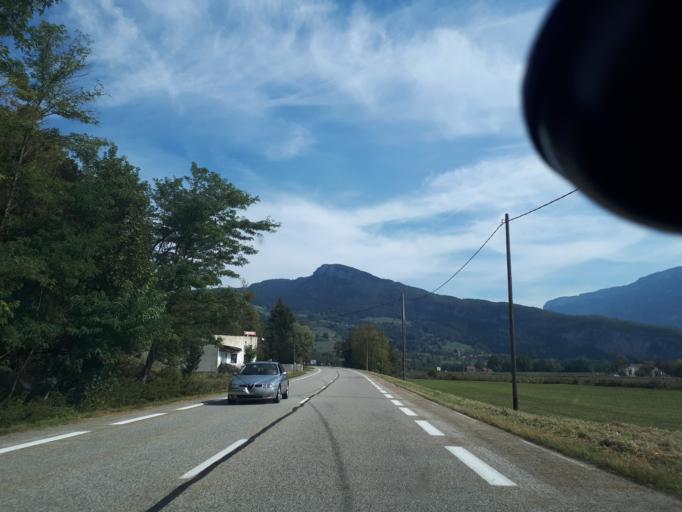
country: FR
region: Rhone-Alpes
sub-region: Departement de la Savoie
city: Les Echelles
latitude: 45.4418
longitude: 5.7602
